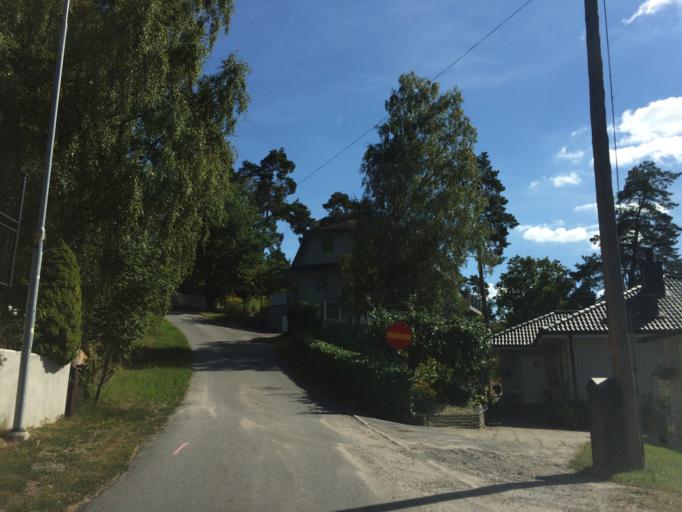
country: SE
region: Stockholm
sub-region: Sollentuna Kommun
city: Sollentuna
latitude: 59.4527
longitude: 17.9088
